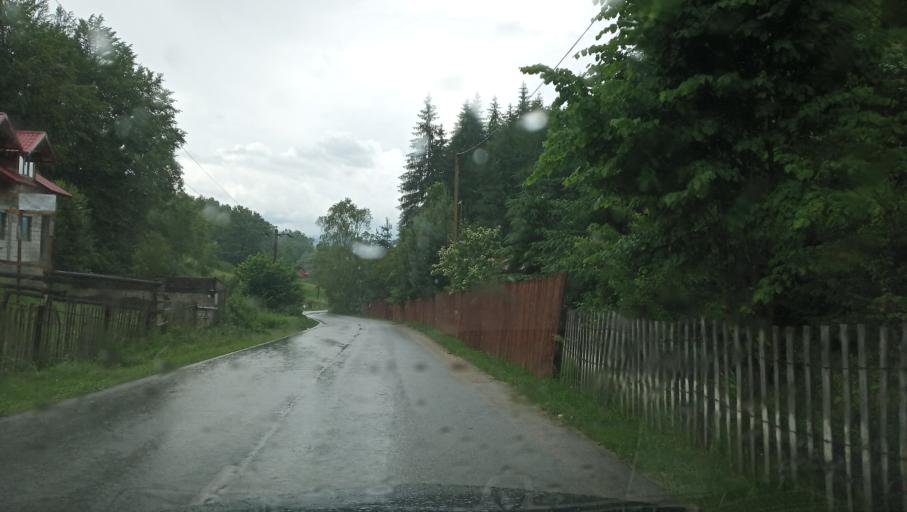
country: RO
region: Hunedoara
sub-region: Oras Petrila
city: Petrila
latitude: 45.3991
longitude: 23.4171
